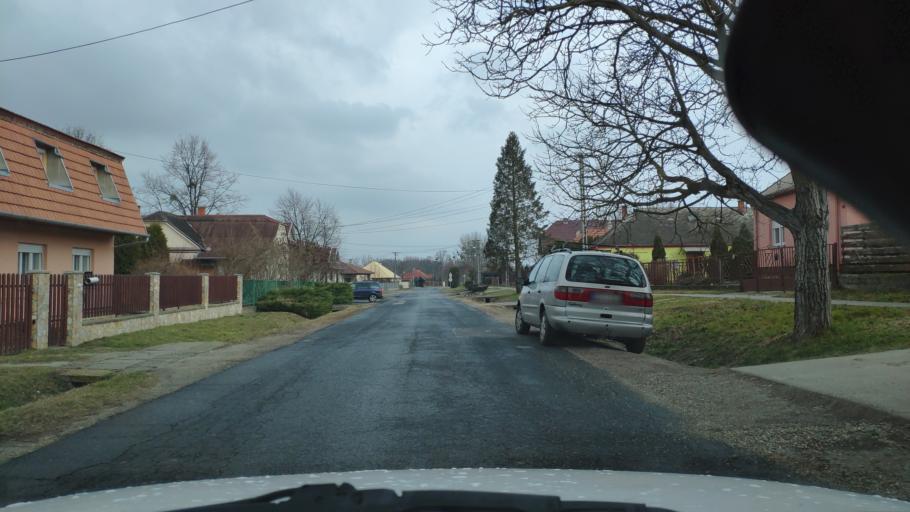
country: HU
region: Zala
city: Nagykanizsa
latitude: 46.4166
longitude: 16.9978
